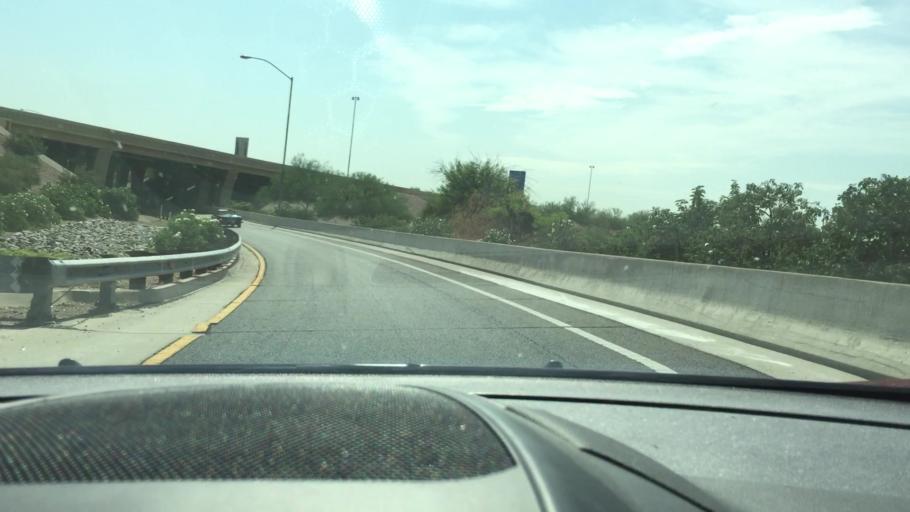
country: US
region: Arizona
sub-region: Maricopa County
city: Tempe Junction
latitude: 33.4547
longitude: -111.9728
